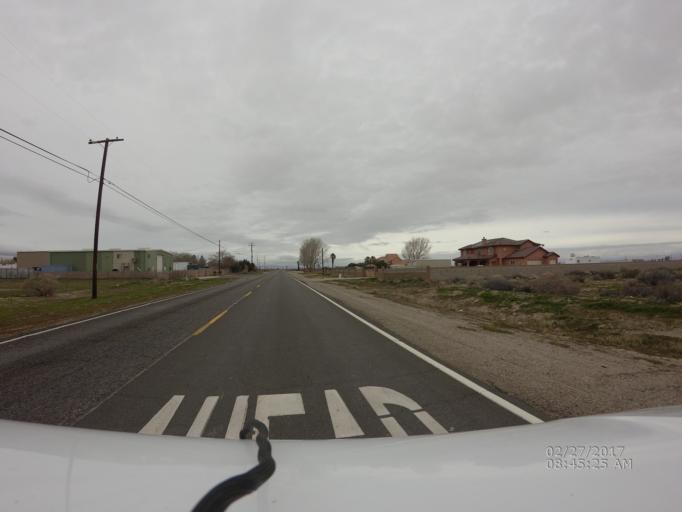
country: US
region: California
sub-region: Los Angeles County
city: Lancaster
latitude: 34.7191
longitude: -118.0748
